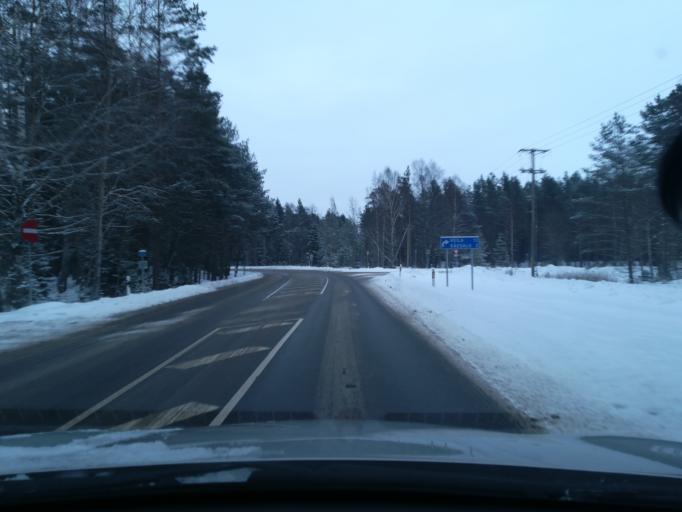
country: EE
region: Harju
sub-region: Keila linn
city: Keila
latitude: 59.3931
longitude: 24.2926
